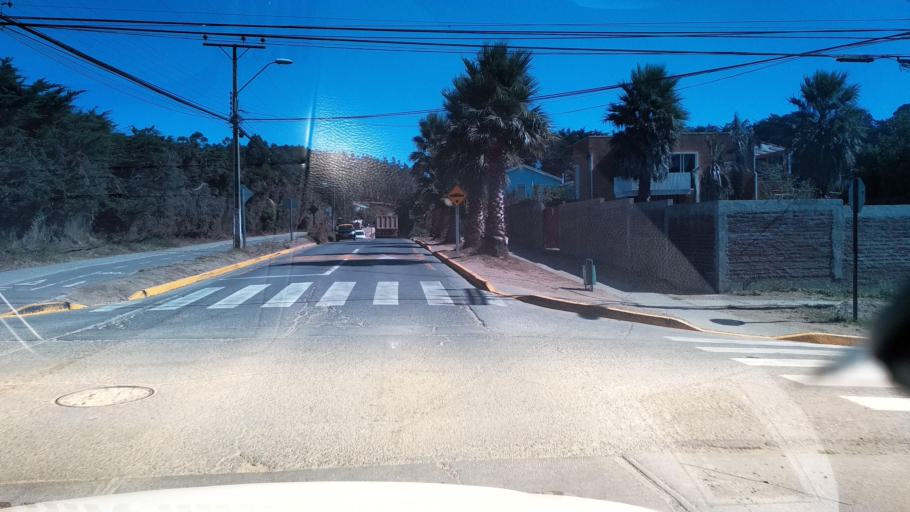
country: CL
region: O'Higgins
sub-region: Provincia de Colchagua
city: Santa Cruz
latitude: -34.3925
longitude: -72.0078
